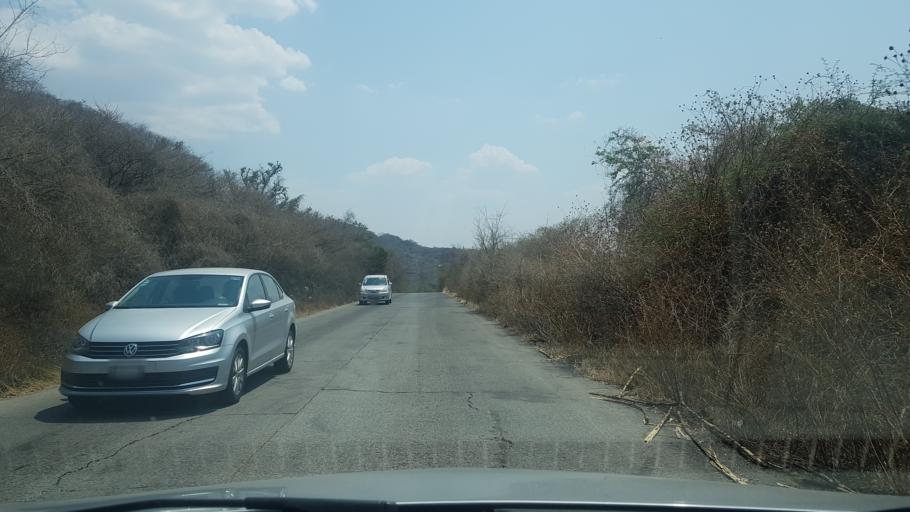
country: MX
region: Morelos
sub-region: Tlaltizapan de Zapata
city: Colonia Palo Prieto (Chipitongo)
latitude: 18.7638
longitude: -99.1078
